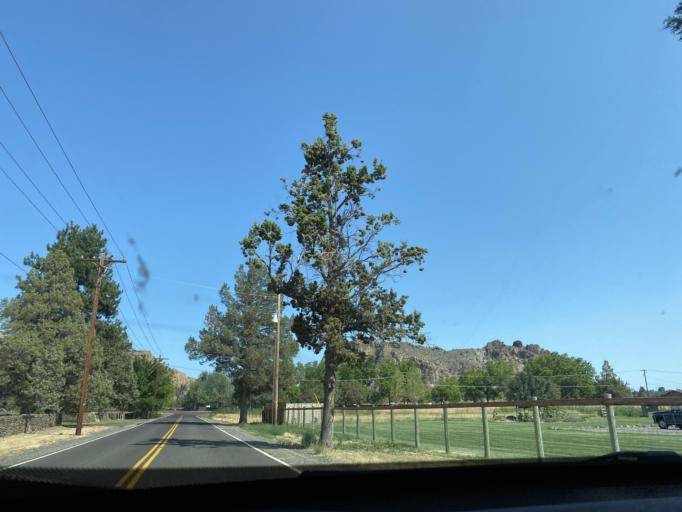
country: US
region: Oregon
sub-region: Deschutes County
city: Terrebonne
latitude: 44.3668
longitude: -121.1608
